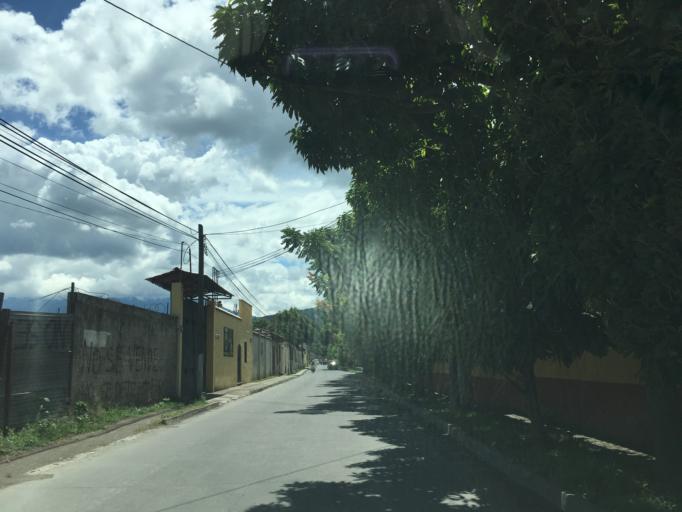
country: GT
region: Sacatepequez
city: Antigua Guatemala
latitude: 14.5436
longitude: -90.7413
